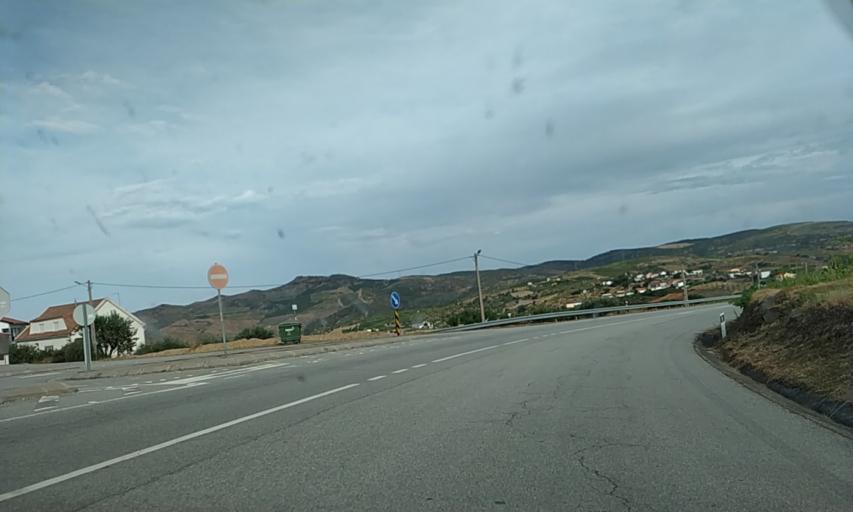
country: PT
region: Viseu
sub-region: Sao Joao da Pesqueira
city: Sao Joao da Pesqueira
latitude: 41.1032
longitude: -7.3834
